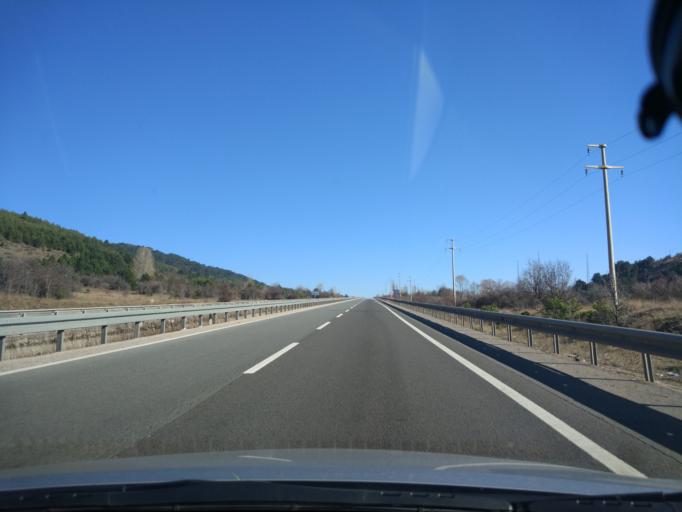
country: TR
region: Bolu
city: Gerede
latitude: 40.8140
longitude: 32.2775
